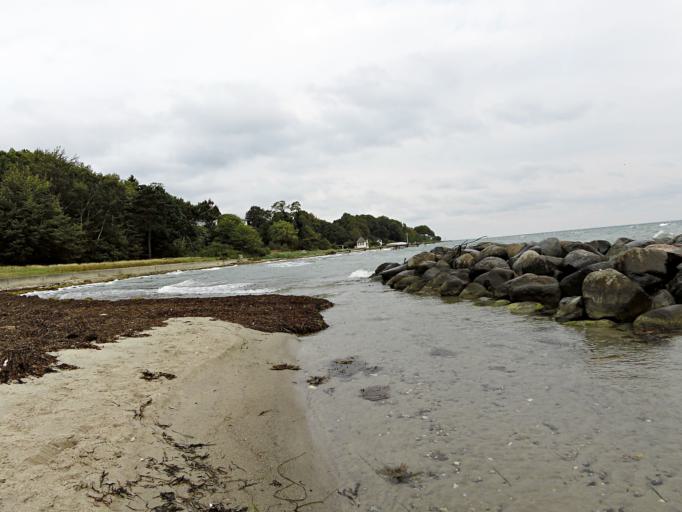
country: DK
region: Capital Region
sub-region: Rudersdal Kommune
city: Trorod
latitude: 55.8338
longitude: 12.5746
